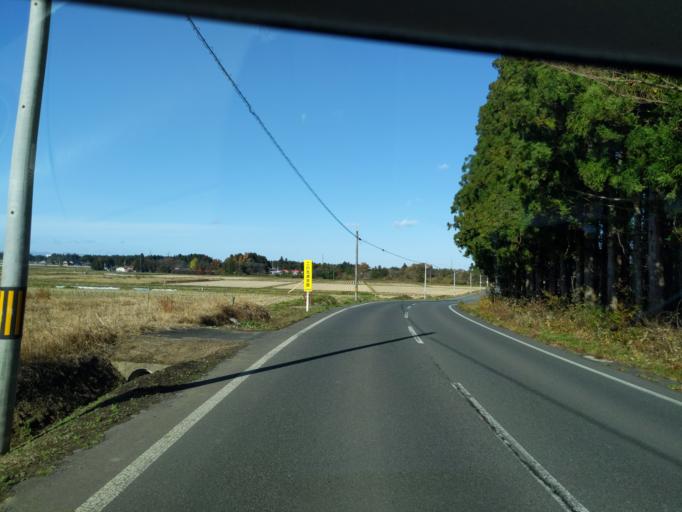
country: JP
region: Iwate
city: Mizusawa
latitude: 39.0871
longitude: 141.0936
